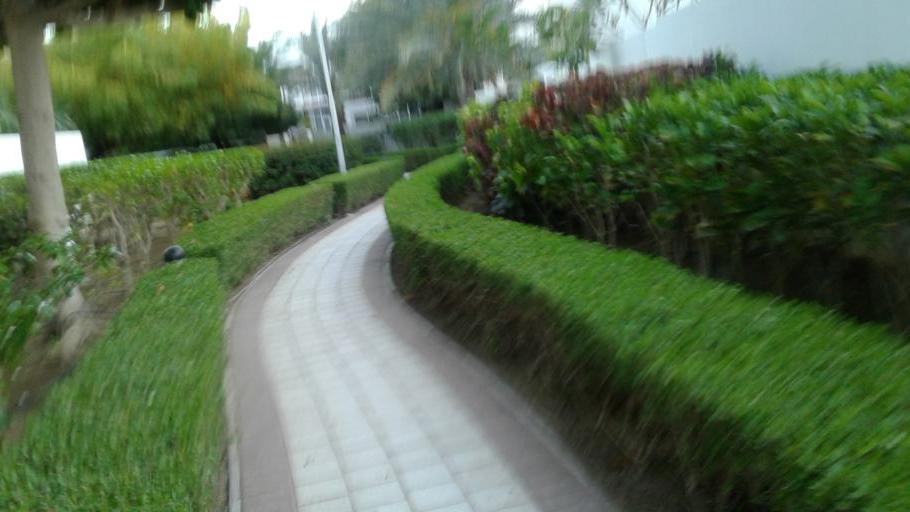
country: OM
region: Muhafazat Masqat
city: As Sib al Jadidah
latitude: 23.6270
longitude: 58.2698
